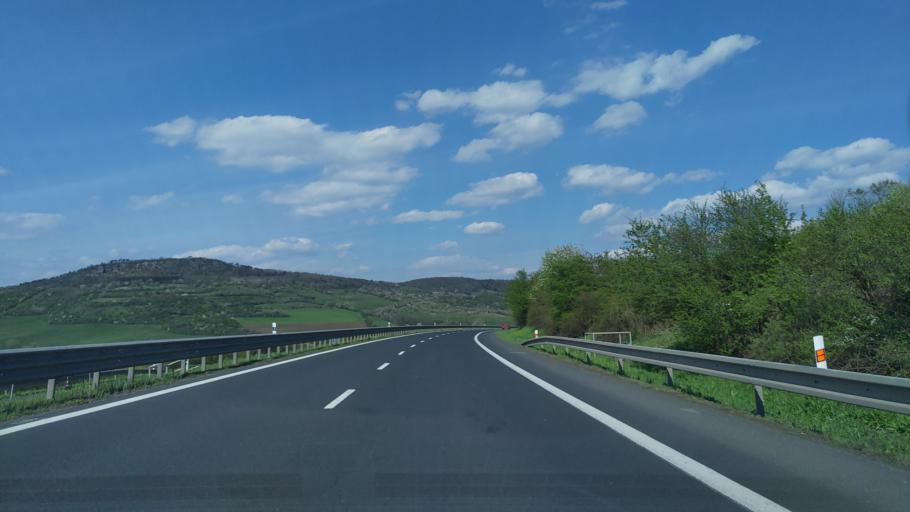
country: CZ
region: Ustecky
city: Branany
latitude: 50.5223
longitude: 13.7118
